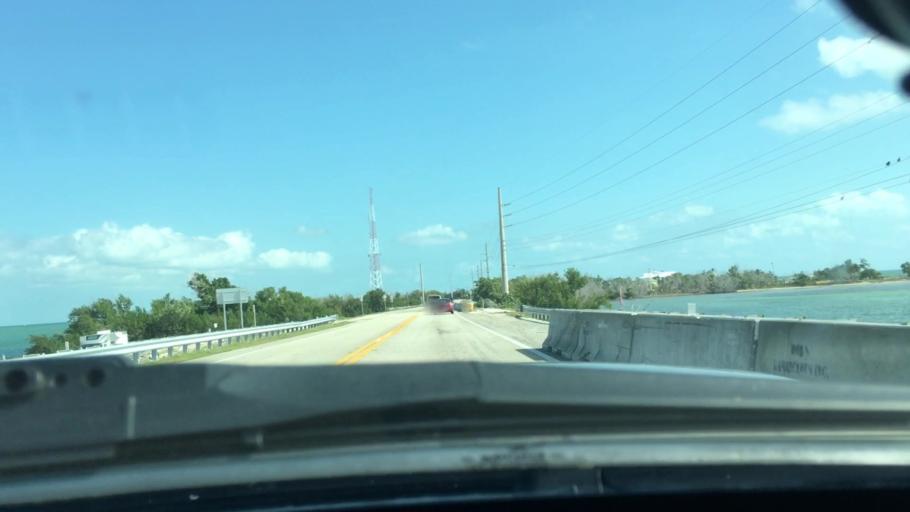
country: US
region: Florida
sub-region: Monroe County
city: Big Pine Key
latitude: 24.6500
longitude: -81.3162
